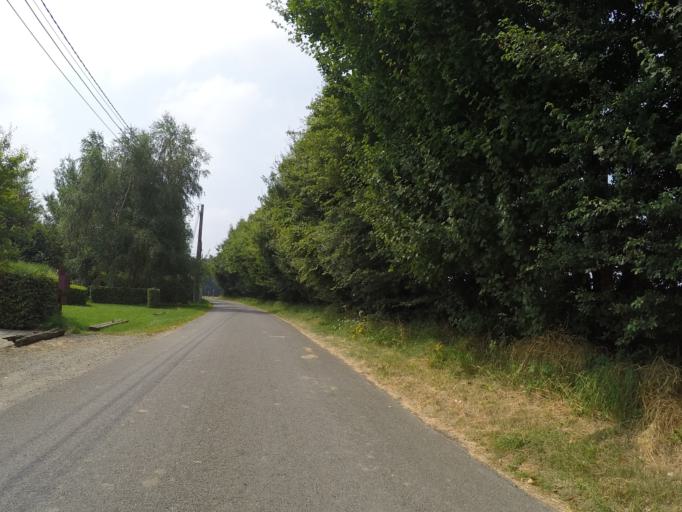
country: BE
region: Wallonia
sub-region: Province de Namur
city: Assesse
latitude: 50.3445
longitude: 4.9856
